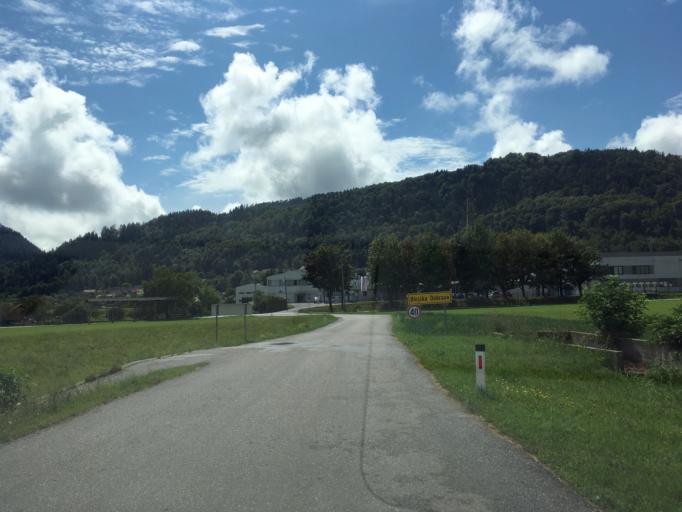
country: SI
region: Bled
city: Zasip
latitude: 46.4102
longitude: 14.1030
